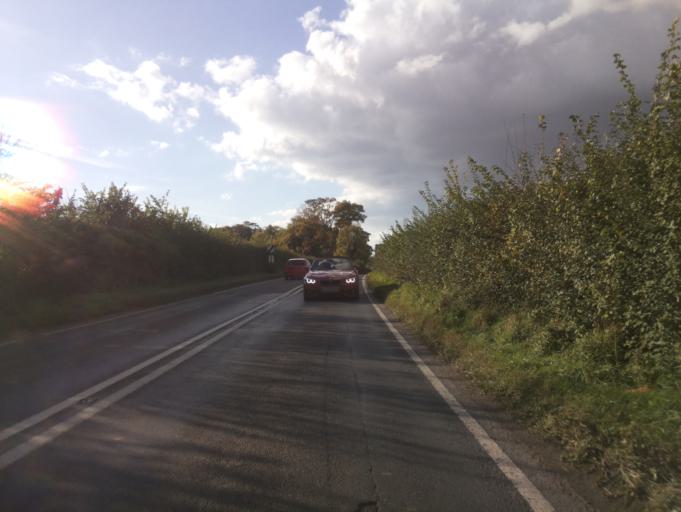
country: GB
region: England
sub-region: Herefordshire
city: Credenhill
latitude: 52.0731
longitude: -2.8095
